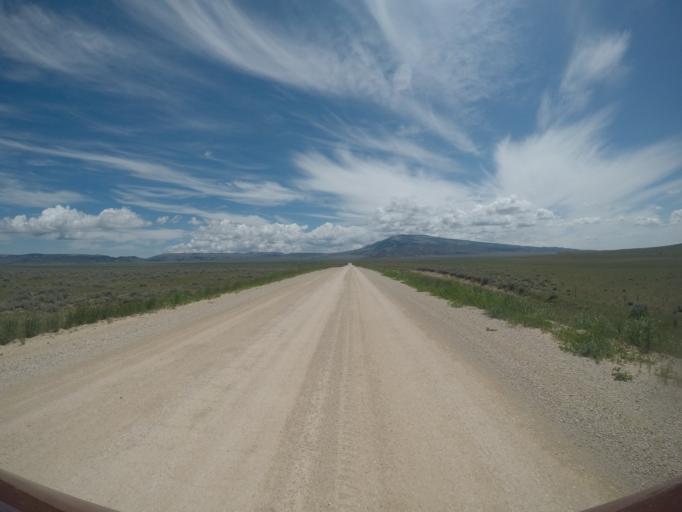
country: US
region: Wyoming
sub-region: Park County
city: Powell
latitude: 45.2051
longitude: -108.7492
